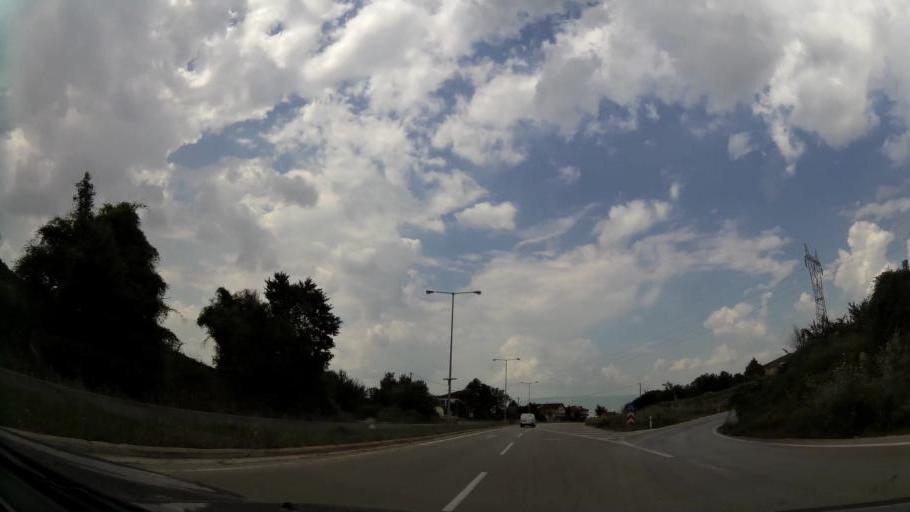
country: GR
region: West Macedonia
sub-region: Nomos Kozanis
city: Koila
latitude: 40.3431
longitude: 21.8250
